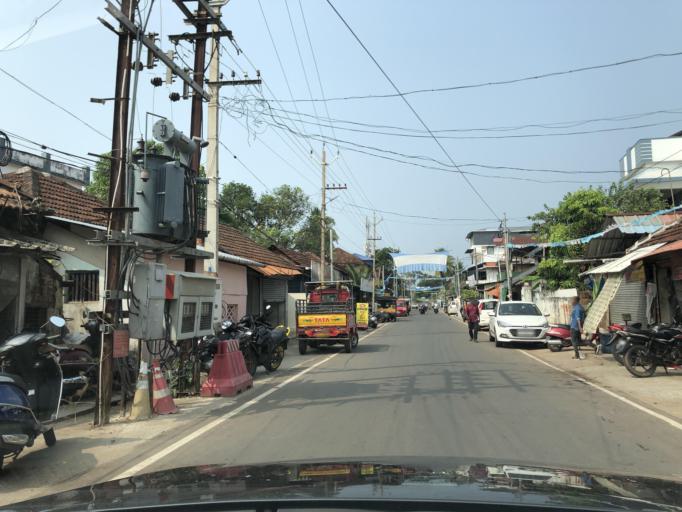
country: IN
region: Kerala
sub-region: Kozhikode
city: Kozhikode
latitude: 11.2615
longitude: 75.7705
